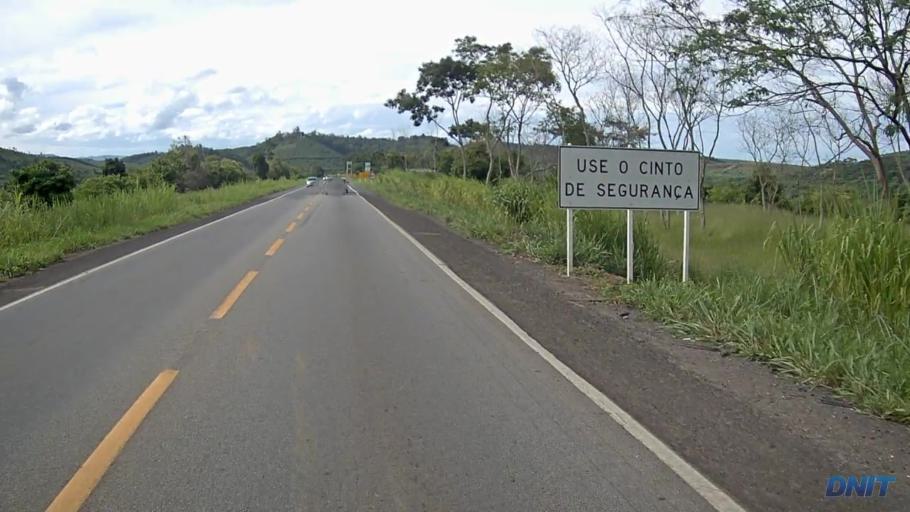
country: BR
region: Minas Gerais
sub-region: Ipaba
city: Ipaba
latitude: -19.2901
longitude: -42.3560
